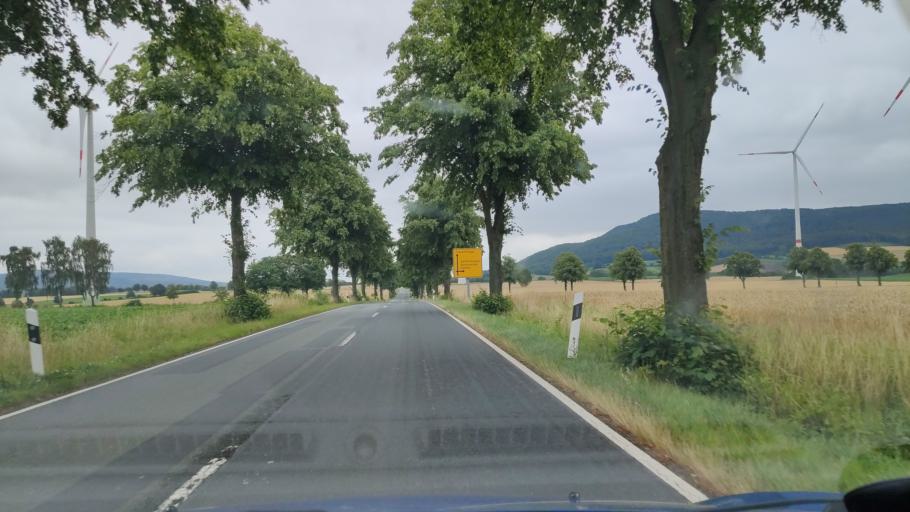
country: DE
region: Lower Saxony
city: Coppenbrugge
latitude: 52.1244
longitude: 9.5038
